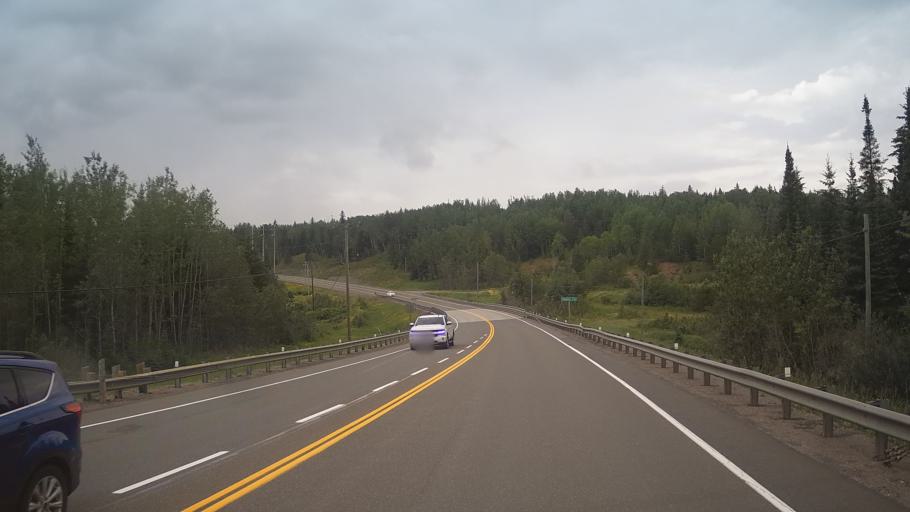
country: CA
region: Ontario
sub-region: Thunder Bay District
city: Thunder Bay
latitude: 48.5352
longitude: -89.5571
